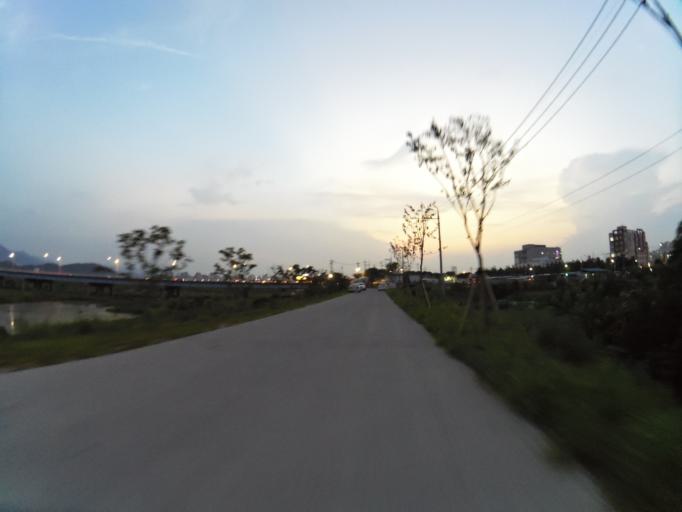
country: KR
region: Gyeongsangbuk-do
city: Gyeongsan-si
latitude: 35.8638
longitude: 128.7166
